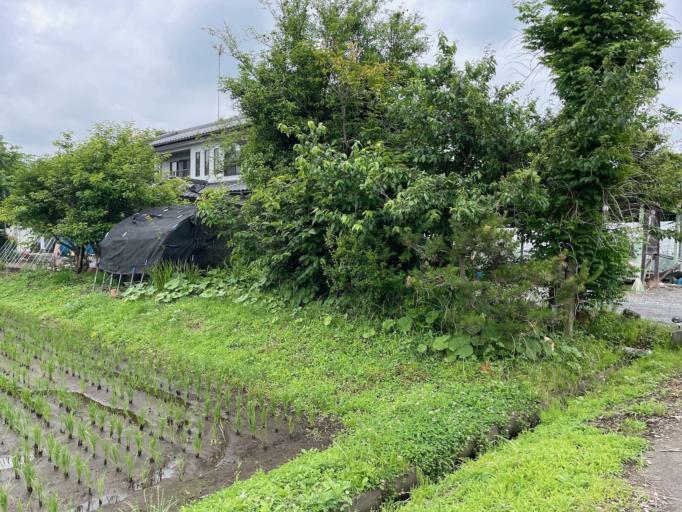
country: JP
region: Tochigi
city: Kanuma
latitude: 36.4871
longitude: 139.7545
